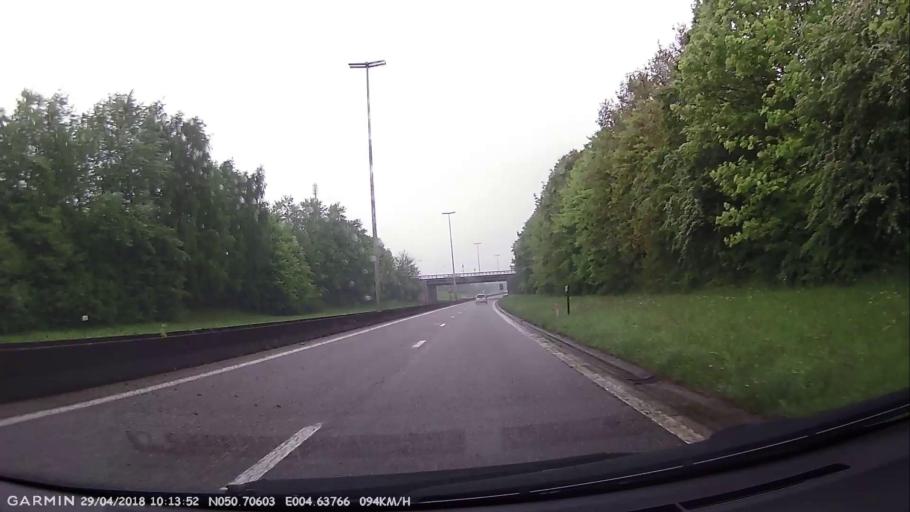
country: BE
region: Wallonia
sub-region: Province du Brabant Wallon
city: Wavre
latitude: 50.7057
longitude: 4.6375
